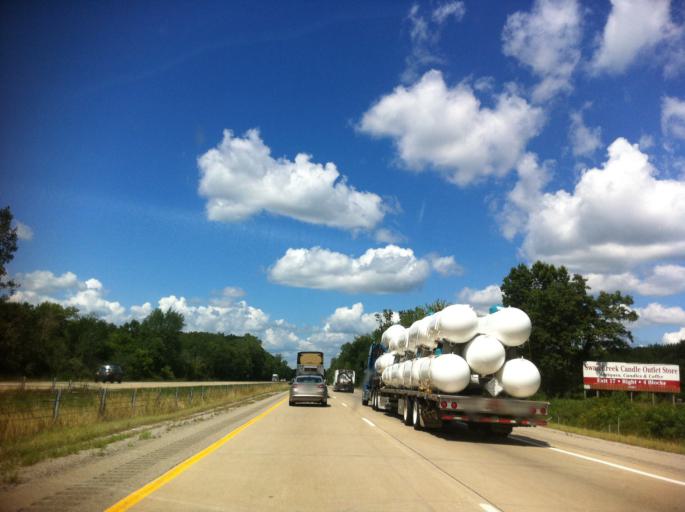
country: US
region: Michigan
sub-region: Monroe County
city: Petersburg
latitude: 41.8776
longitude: -83.6611
